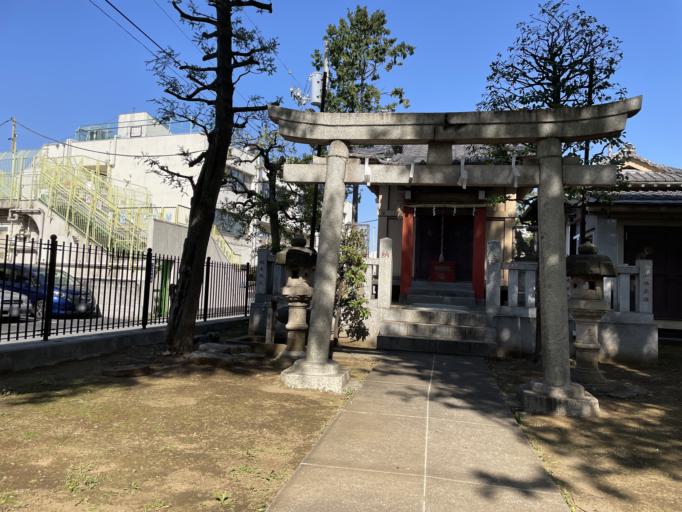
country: JP
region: Saitama
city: Kawaguchi
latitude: 35.7528
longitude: 139.6941
